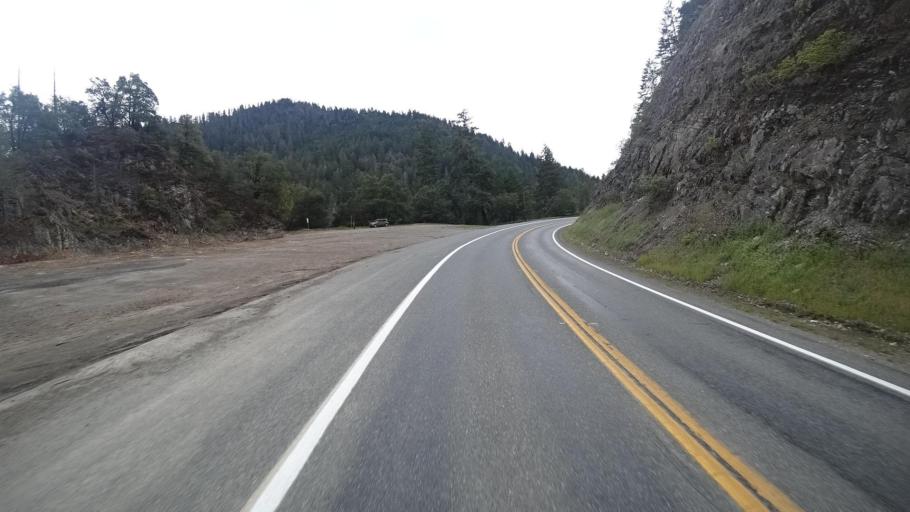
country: US
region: California
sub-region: Humboldt County
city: Willow Creek
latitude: 40.9994
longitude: -123.6259
